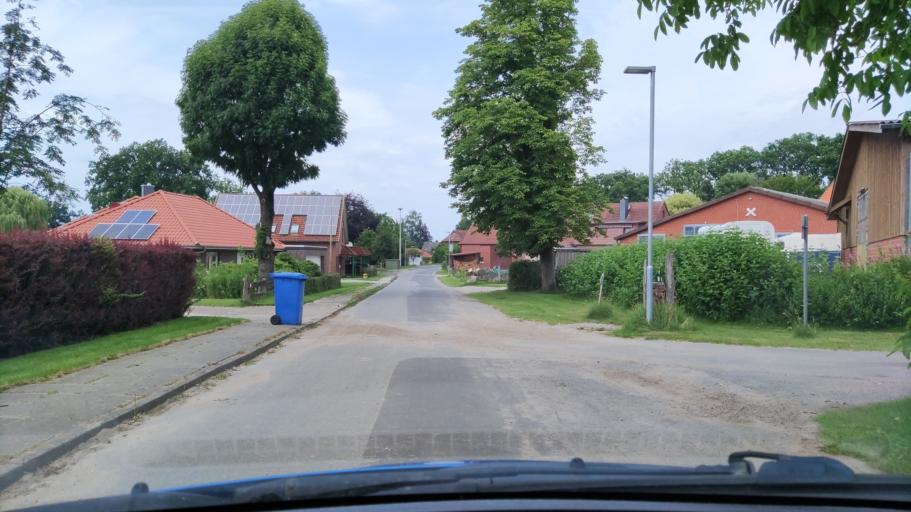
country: DE
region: Lower Saxony
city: Hanstedt
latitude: 53.2357
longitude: 10.0273
